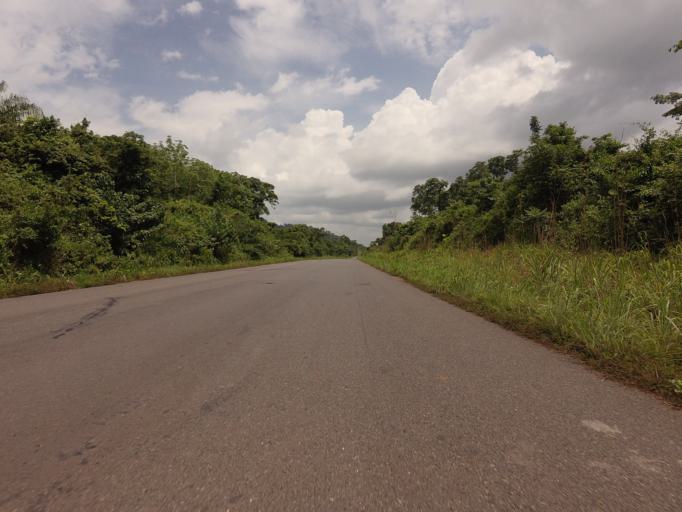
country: GH
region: Volta
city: Ho
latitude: 6.4844
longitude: 0.1975
